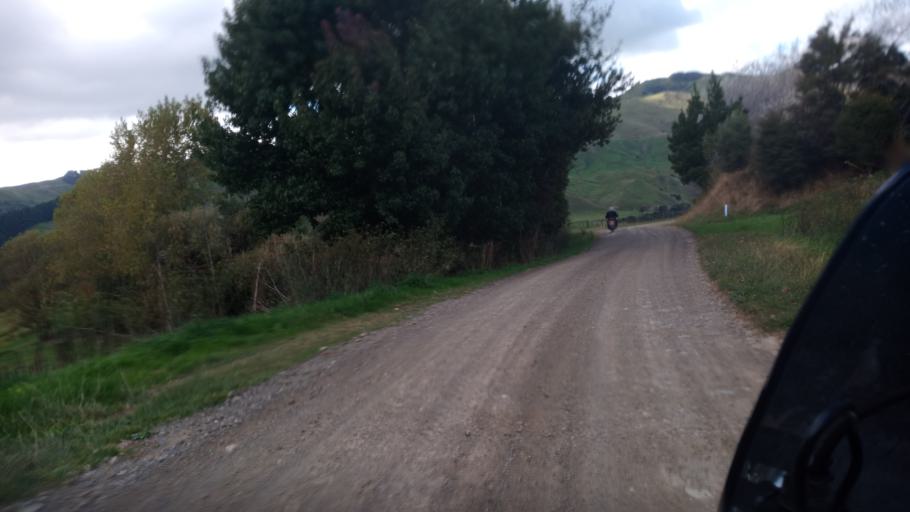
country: NZ
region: Gisborne
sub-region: Gisborne District
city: Gisborne
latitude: -38.4600
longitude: 177.6329
